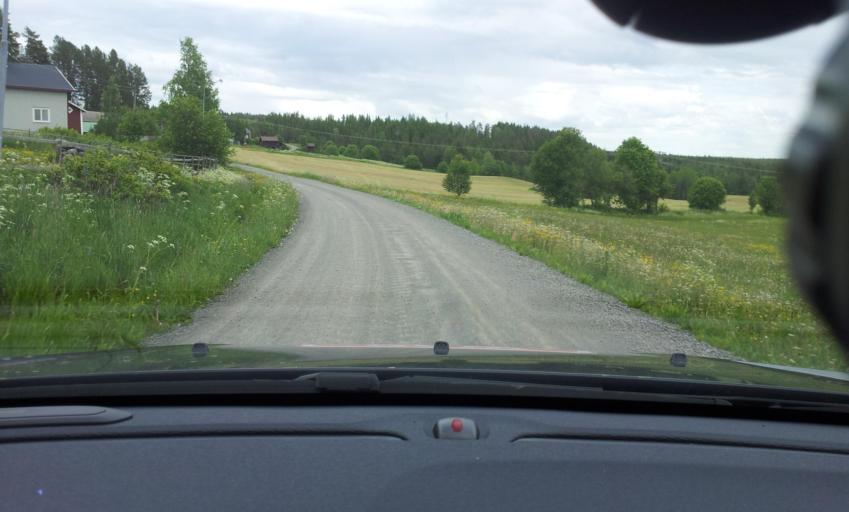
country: SE
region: Jaemtland
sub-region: OEstersunds Kommun
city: Brunflo
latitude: 62.9648
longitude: 14.7094
